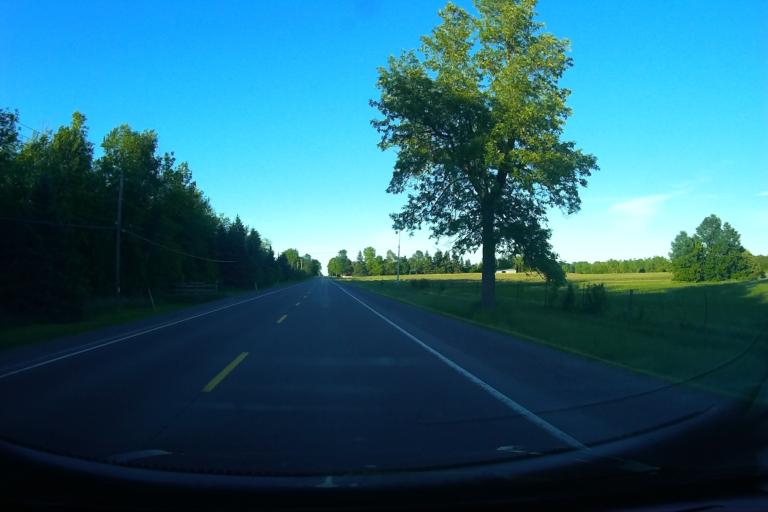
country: CA
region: Ontario
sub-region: Lanark County
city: Smiths Falls
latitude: 44.9846
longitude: -75.7231
